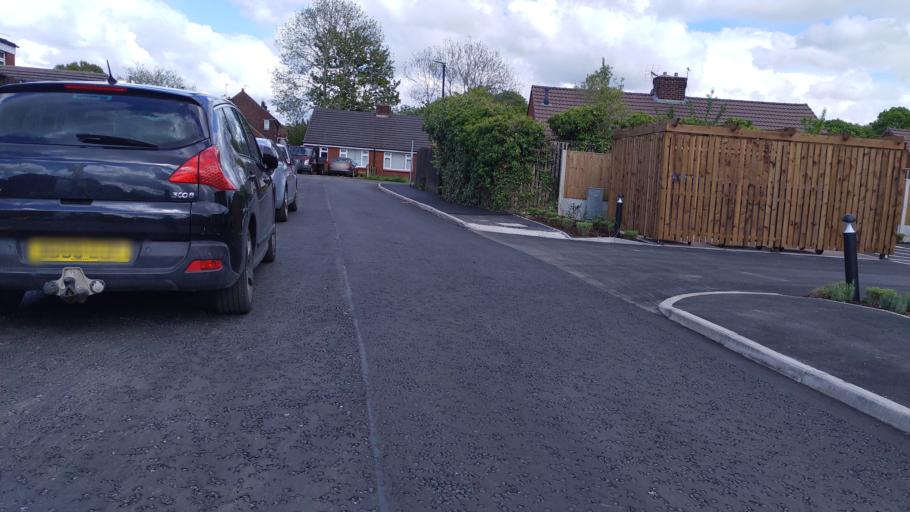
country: GB
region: England
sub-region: Lancashire
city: Euxton
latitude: 53.6673
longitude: -2.6808
